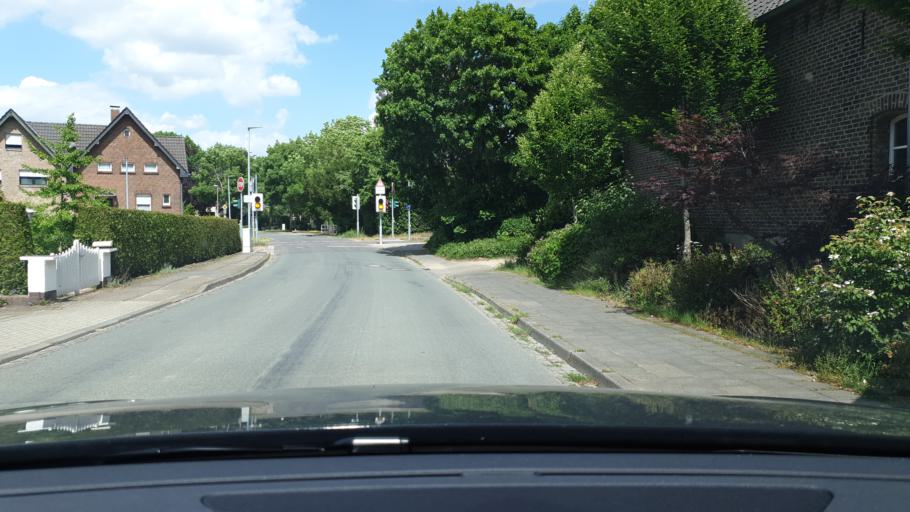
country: DE
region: North Rhine-Westphalia
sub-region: Regierungsbezirk Dusseldorf
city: Kleve
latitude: 51.8023
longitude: 6.0957
